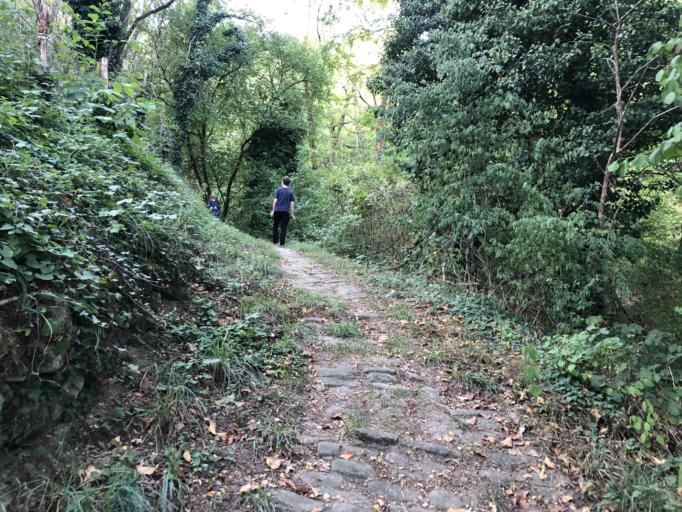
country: IT
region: Emilia-Romagna
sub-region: Forli-Cesena
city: Portico e San Benedetto
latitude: 44.0235
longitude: 11.7817
